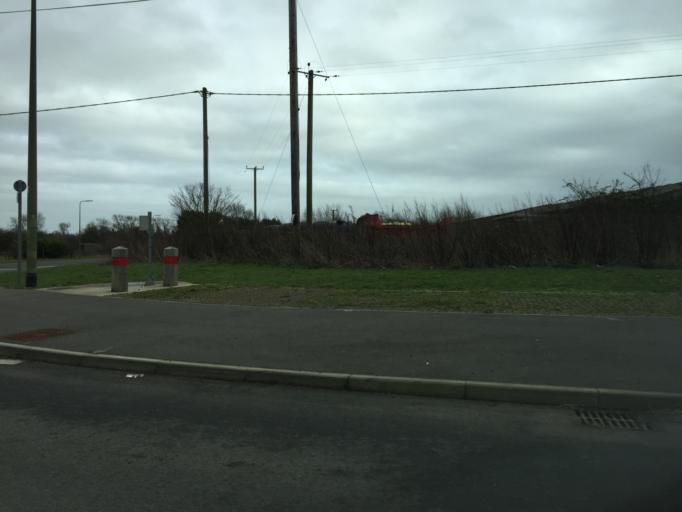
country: GB
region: England
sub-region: Oxfordshire
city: Harwell
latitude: 51.5842
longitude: -1.2705
